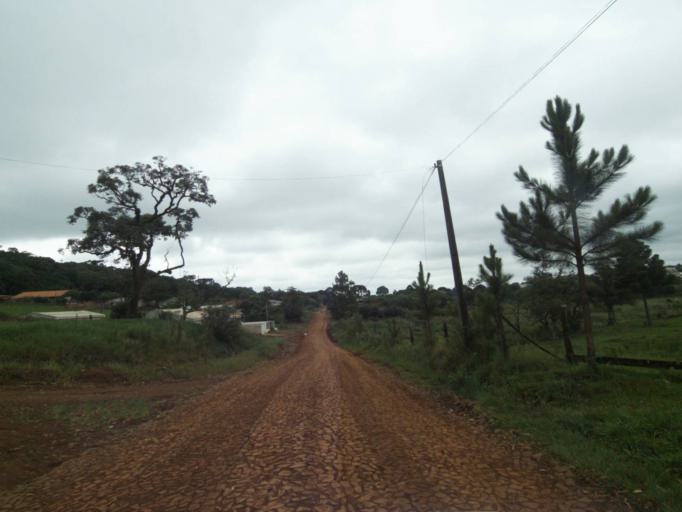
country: BR
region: Parana
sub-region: Pitanga
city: Pitanga
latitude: -24.9327
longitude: -51.8681
